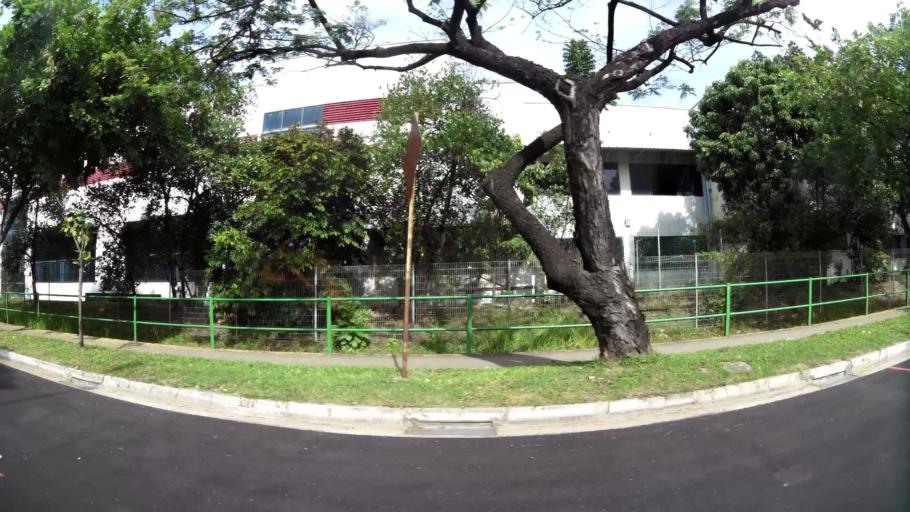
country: MY
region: Johor
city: Johor Bahru
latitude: 1.3131
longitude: 103.6545
